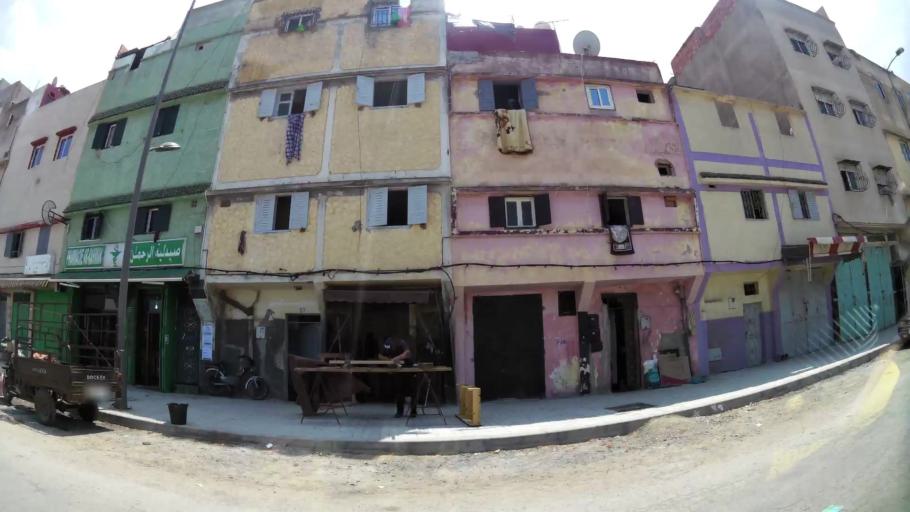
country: MA
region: Rabat-Sale-Zemmour-Zaer
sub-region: Rabat
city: Rabat
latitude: 33.9860
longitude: -6.8824
